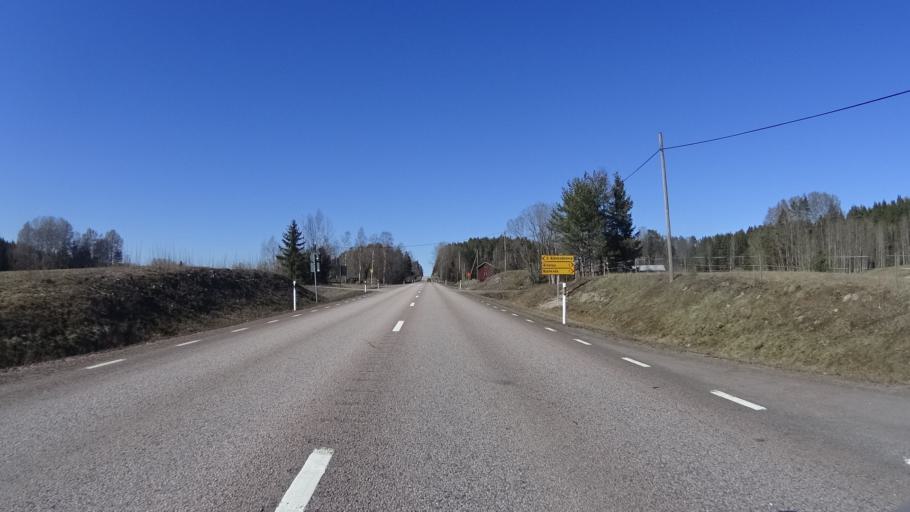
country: SE
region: Vaermland
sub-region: Karlstads Kommun
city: Edsvalla
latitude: 59.5797
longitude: 13.0174
